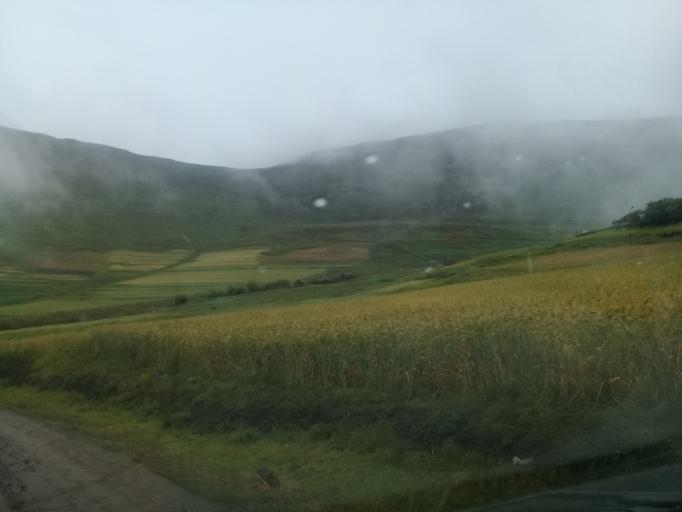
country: LS
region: Mokhotlong
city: Mokhotlong
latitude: -29.3874
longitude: 28.9771
